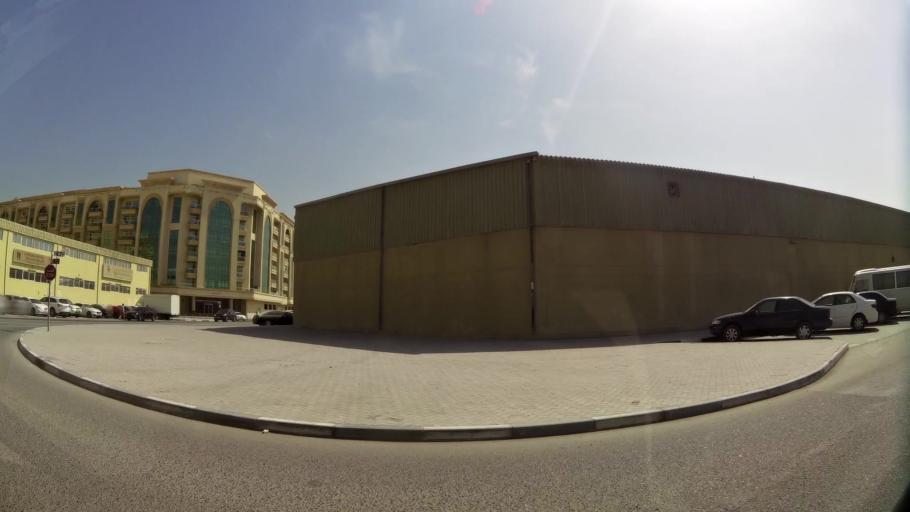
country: AE
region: Ash Shariqah
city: Sharjah
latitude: 25.2803
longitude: 55.3889
